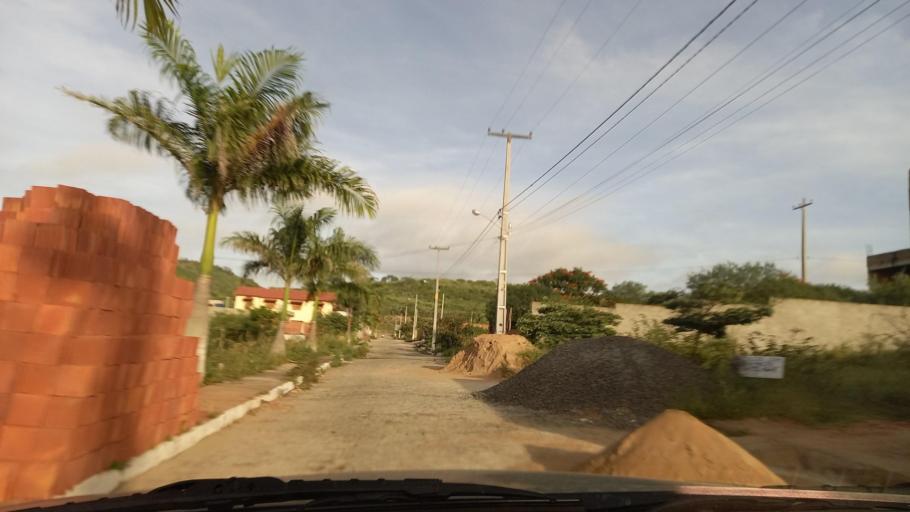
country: BR
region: Pernambuco
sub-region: Bezerros
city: Bezerros
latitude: -8.2169
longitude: -35.7505
